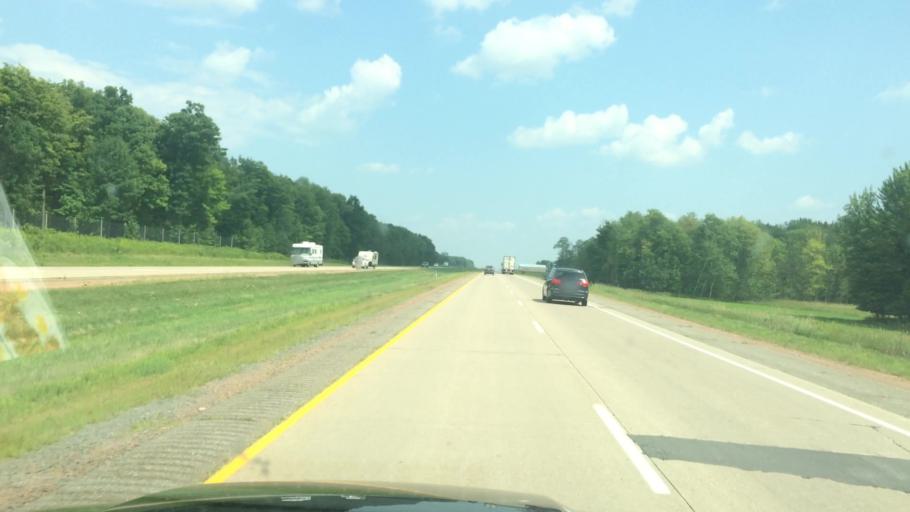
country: US
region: Wisconsin
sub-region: Marathon County
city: Athens
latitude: 44.9452
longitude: -90.1528
